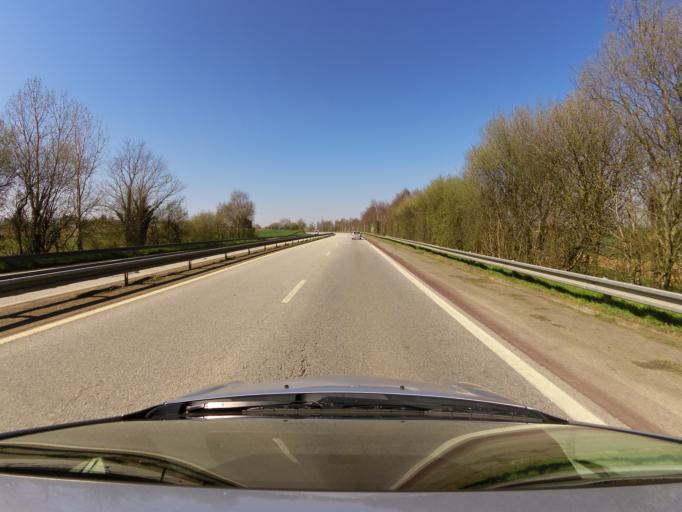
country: FR
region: Brittany
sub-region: Departement du Morbihan
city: Guegon
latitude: 47.9433
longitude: -2.6053
